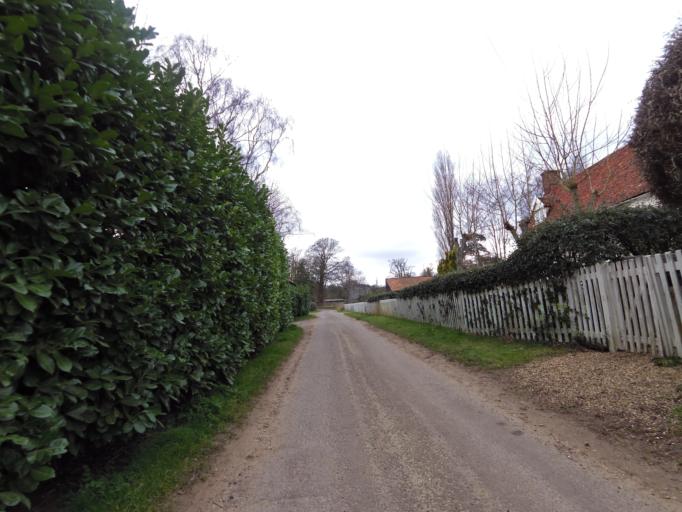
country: GB
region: England
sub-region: Suffolk
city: Woodbridge
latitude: 52.0578
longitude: 1.3246
